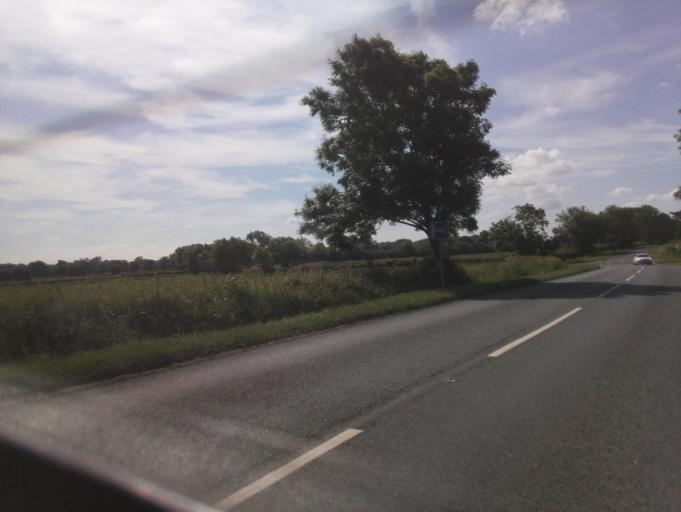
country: GB
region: England
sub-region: Lincolnshire
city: Skellingthorpe
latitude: 53.1600
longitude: -0.6379
